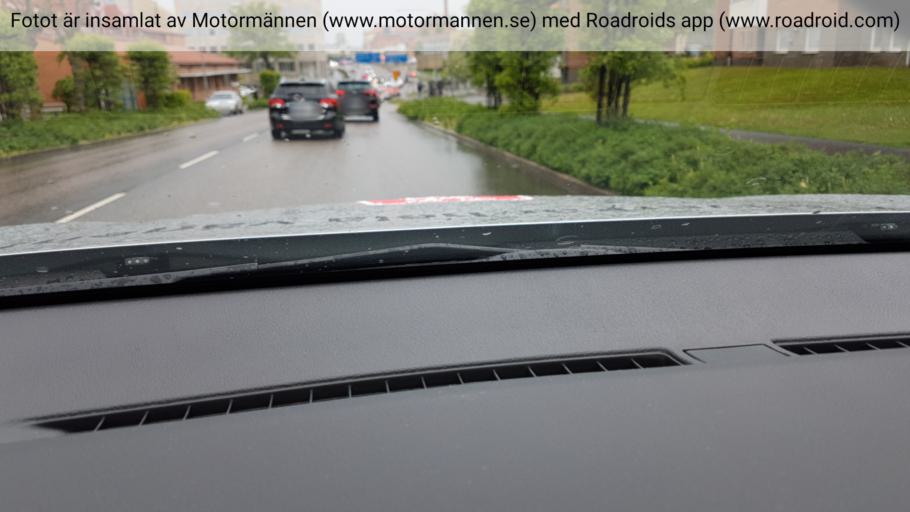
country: SE
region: Vaestra Goetaland
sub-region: Skovde Kommun
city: Skoevde
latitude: 58.3939
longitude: 13.8527
